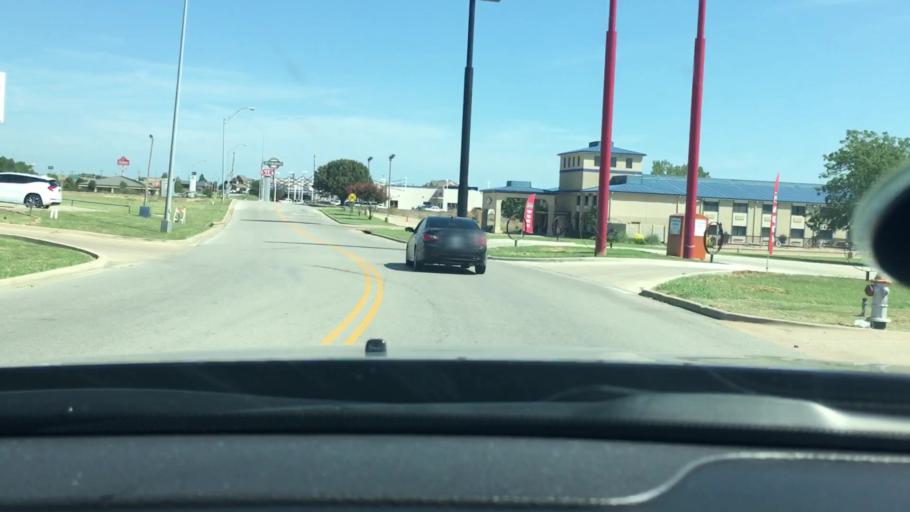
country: US
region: Oklahoma
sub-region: Carter County
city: Ardmore
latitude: 34.1761
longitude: -97.1662
